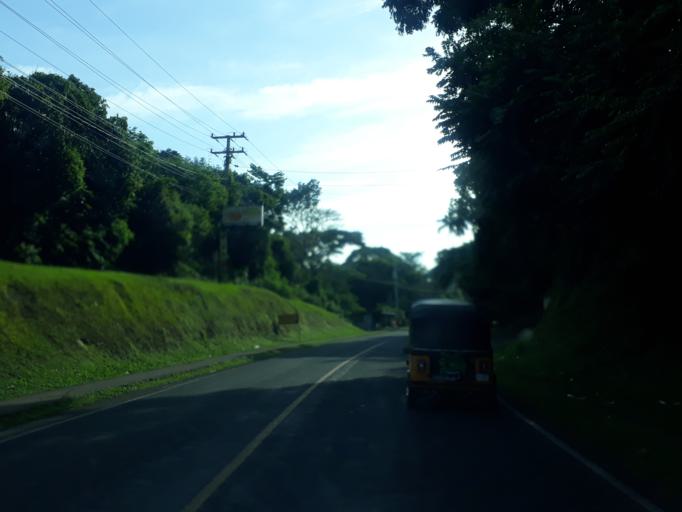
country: NI
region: Masaya
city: Masatepe
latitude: 11.9049
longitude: -86.1535
